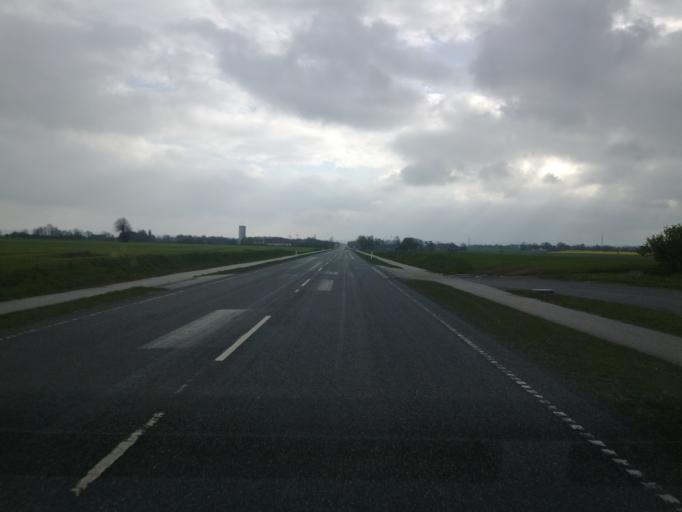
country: DK
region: North Denmark
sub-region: Frederikshavn Kommune
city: Saeby
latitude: 57.2951
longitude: 10.3980
